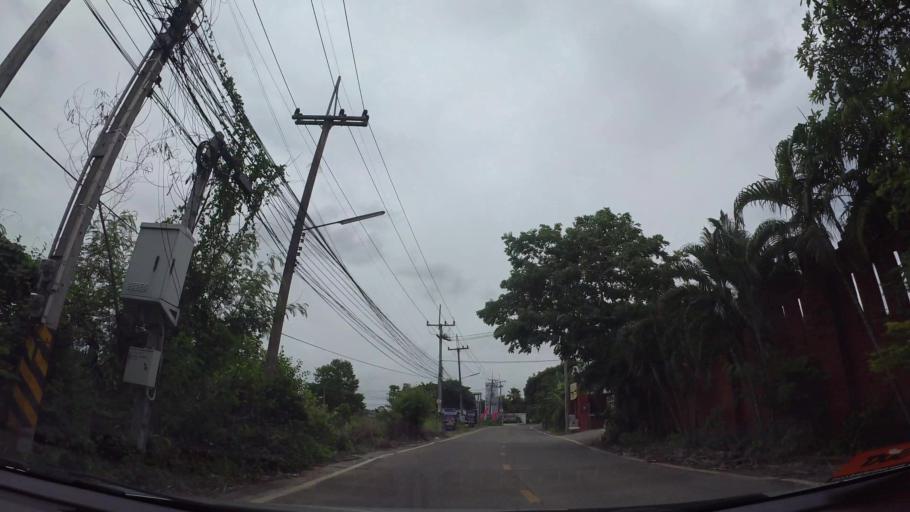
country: TH
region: Chon Buri
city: Si Racha
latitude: 13.1689
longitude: 100.9740
